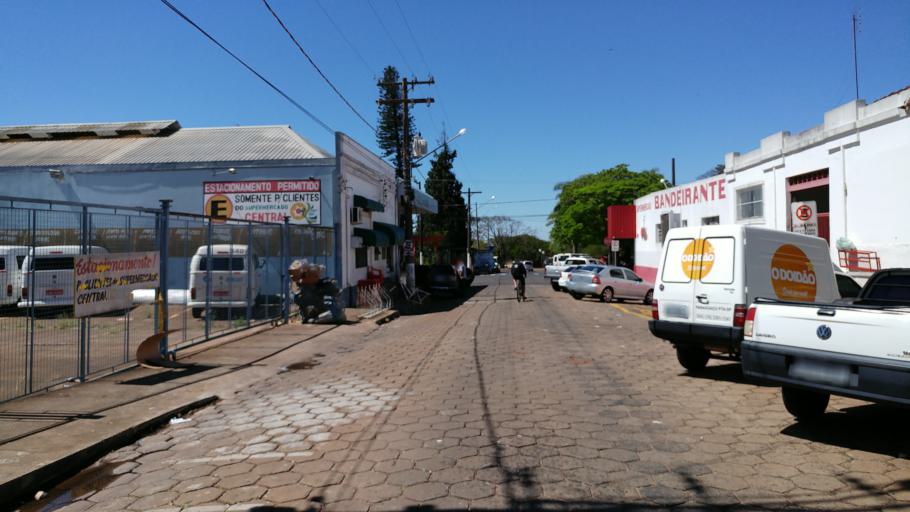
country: BR
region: Sao Paulo
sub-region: Paraguacu Paulista
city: Paraguacu Paulista
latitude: -22.4134
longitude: -50.5737
